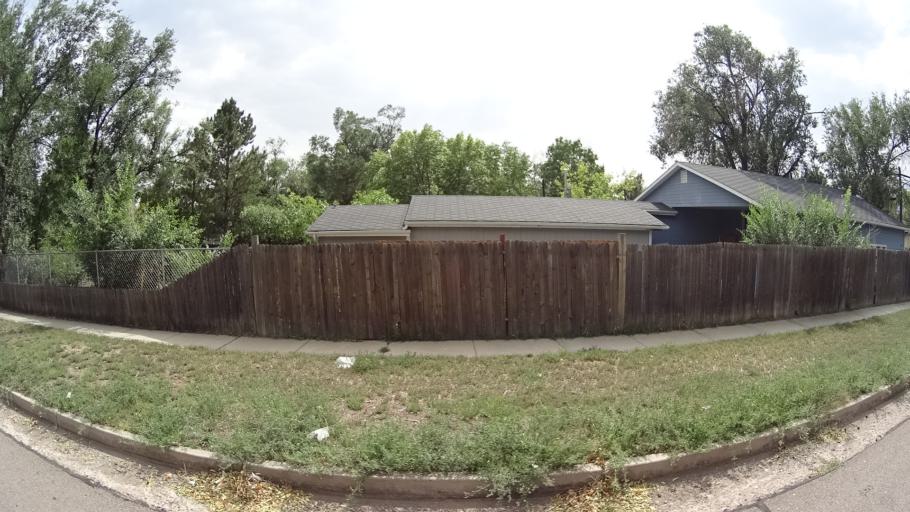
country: US
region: Colorado
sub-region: El Paso County
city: Colorado Springs
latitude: 38.8436
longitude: -104.7905
